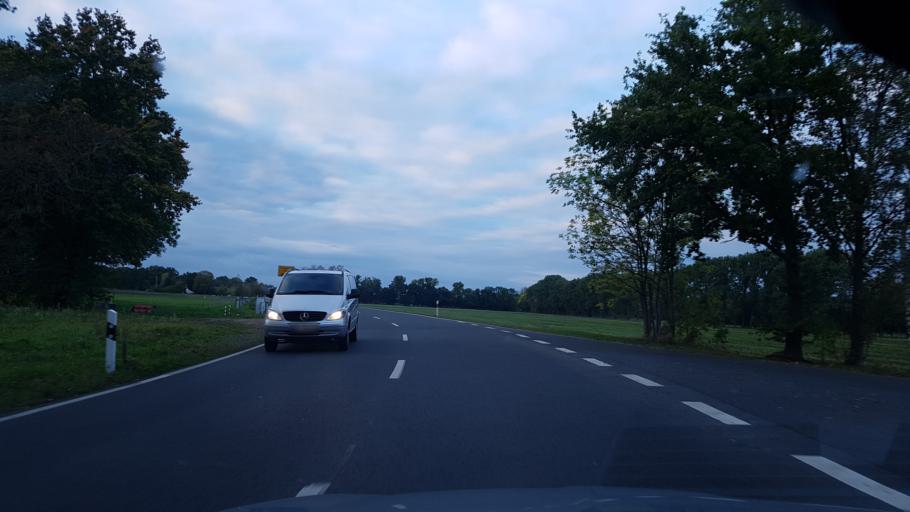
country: DE
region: Saxony
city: Ebersbach
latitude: 51.2815
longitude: 13.6219
